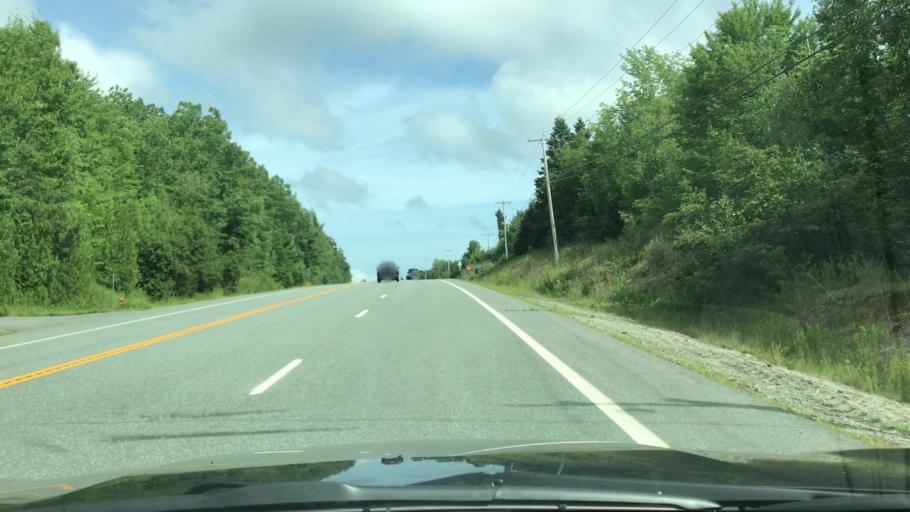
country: US
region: Maine
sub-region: Hancock County
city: Surry
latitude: 44.5470
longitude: -68.5229
